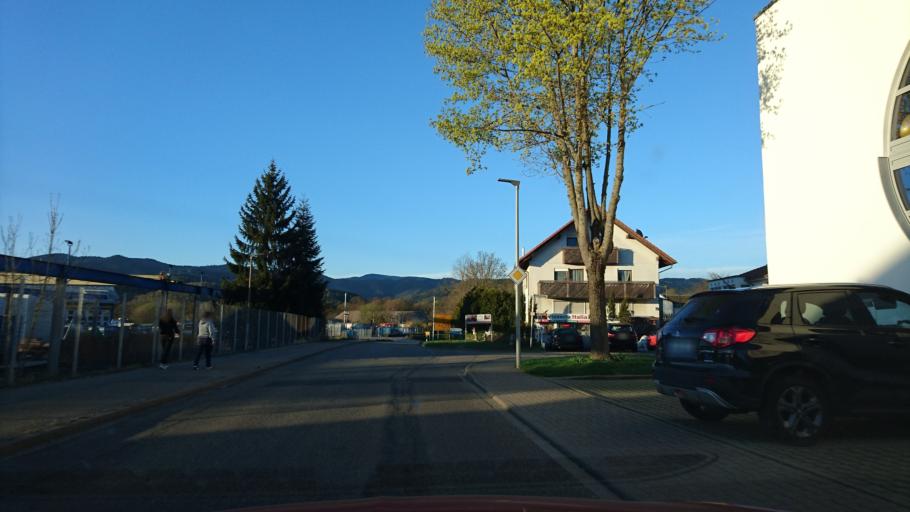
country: DE
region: Baden-Wuerttemberg
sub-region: Freiburg Region
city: Kirchzarten
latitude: 47.9704
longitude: 7.9586
